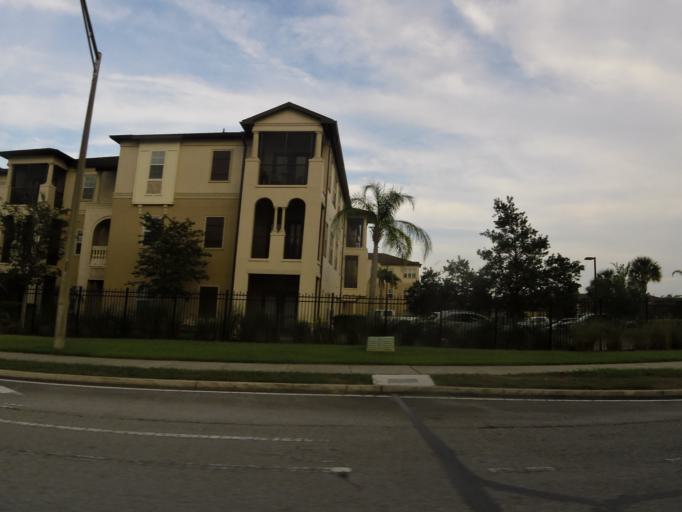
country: US
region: Florida
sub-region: Saint Johns County
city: Ponte Vedra Beach
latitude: 30.2206
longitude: -81.5094
